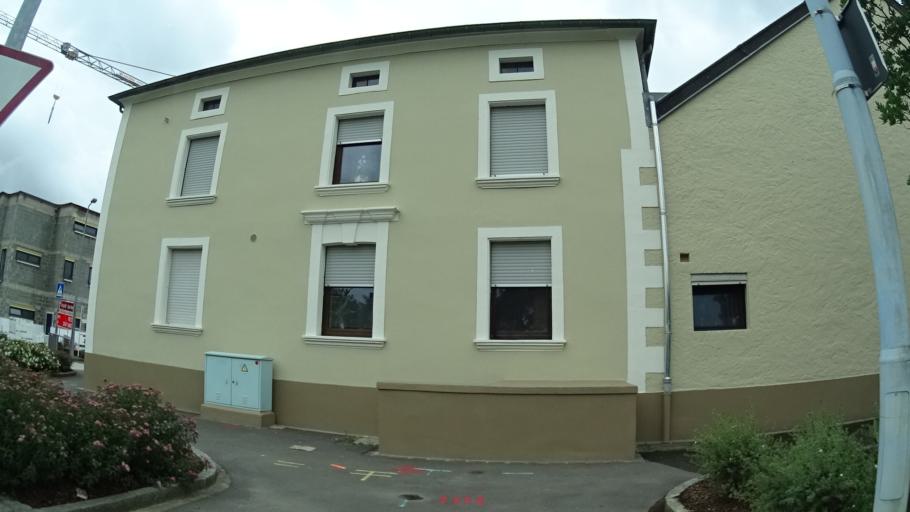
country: LU
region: Luxembourg
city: Pontpierre
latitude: 49.5361
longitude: 6.0269
